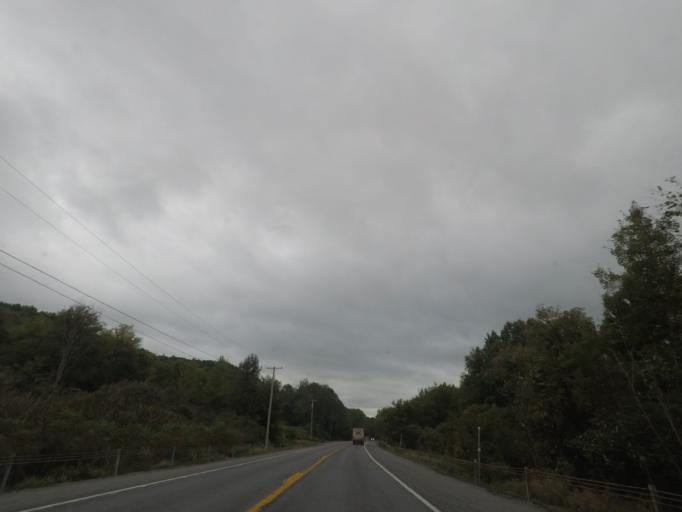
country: US
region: New York
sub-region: Rensselaer County
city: Hoosick Falls
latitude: 42.9435
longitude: -73.3677
